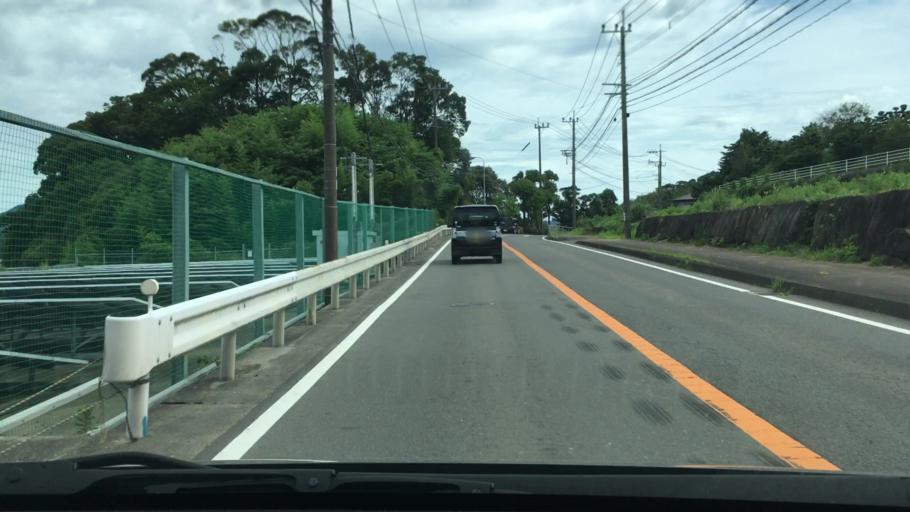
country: JP
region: Nagasaki
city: Togitsu
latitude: 32.8840
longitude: 129.7901
